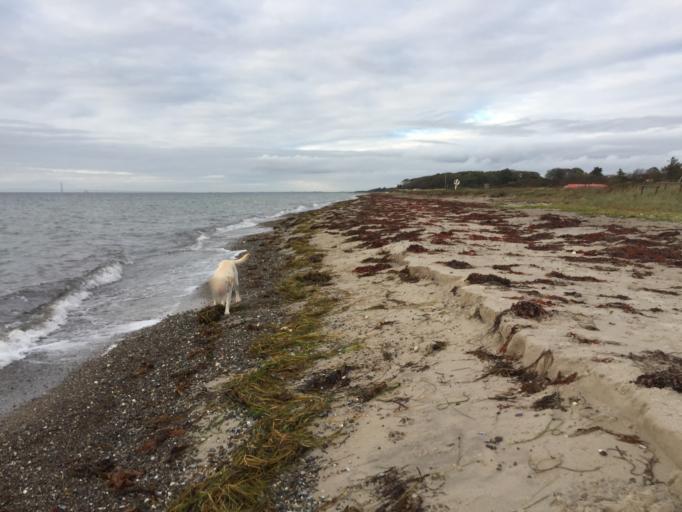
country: DK
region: Zealand
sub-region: Slagelse Kommune
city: Korsor
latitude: 55.2168
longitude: 11.1721
